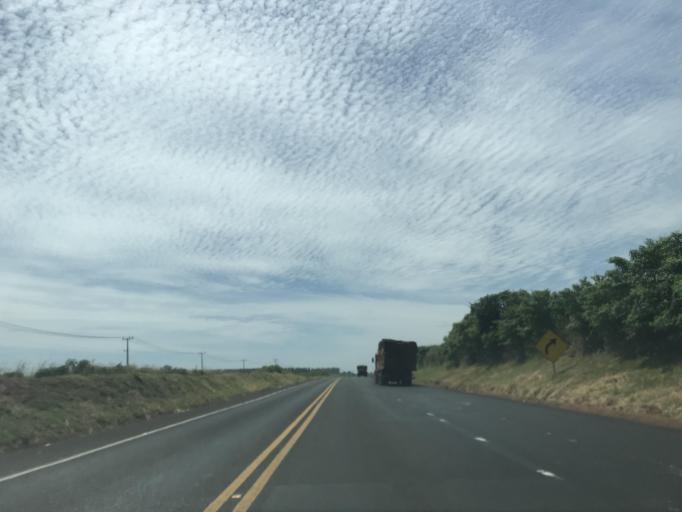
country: BR
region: Parana
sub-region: Paranavai
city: Paranavai
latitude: -23.0033
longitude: -52.5535
